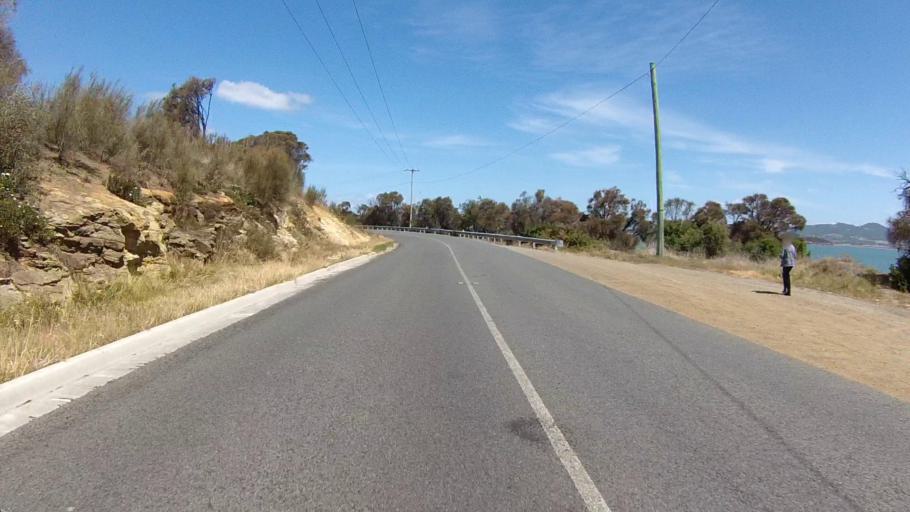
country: AU
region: Tasmania
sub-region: Sorell
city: Sorell
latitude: -42.7893
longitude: 147.5220
